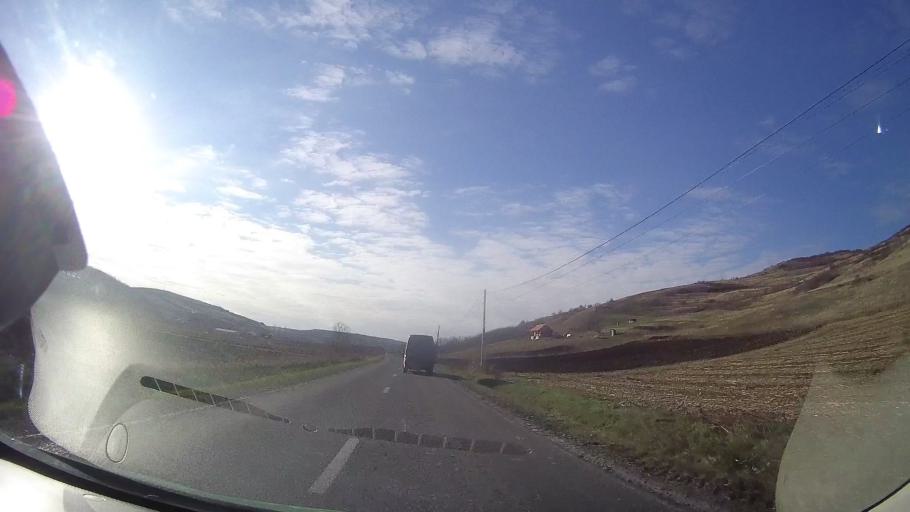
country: RO
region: Cluj
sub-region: Comuna Caianu
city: Caianu
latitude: 46.7997
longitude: 23.9238
